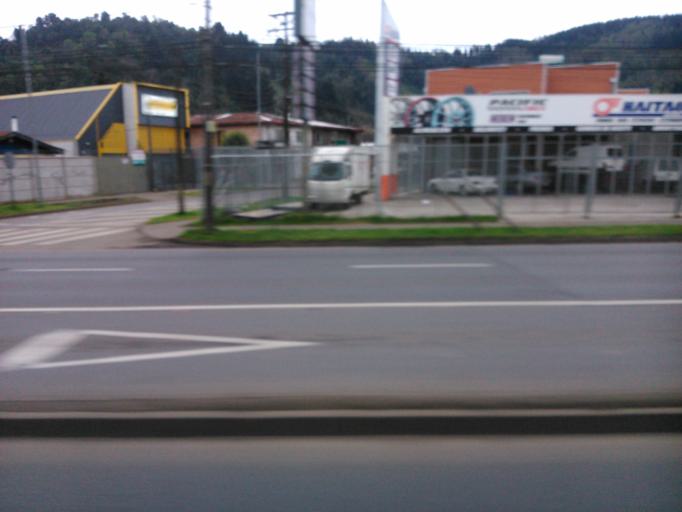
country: CL
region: Araucania
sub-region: Provincia de Cautin
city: Temuco
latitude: -38.7261
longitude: -72.5752
